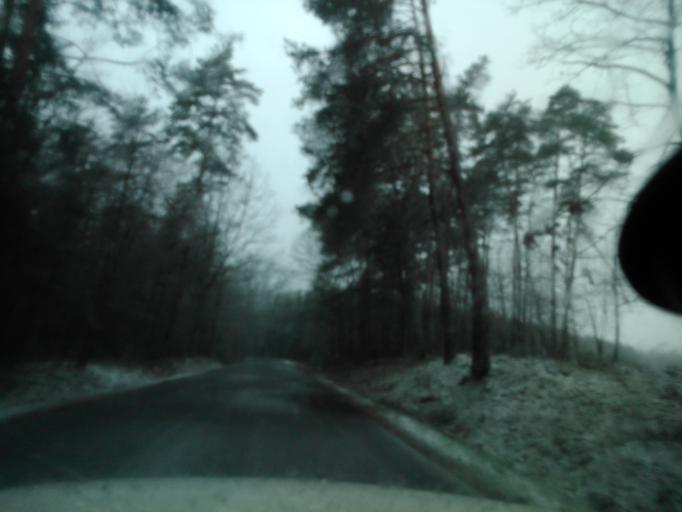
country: PL
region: Warmian-Masurian Voivodeship
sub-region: Powiat dzialdowski
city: Rybno
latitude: 53.3297
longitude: 19.9313
